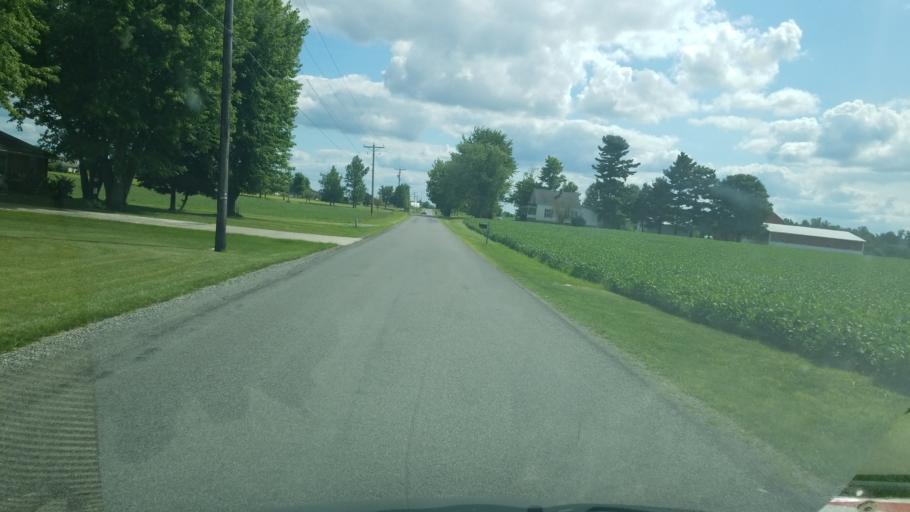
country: US
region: Ohio
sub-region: Allen County
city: Lima
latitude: 40.7589
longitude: -83.9942
